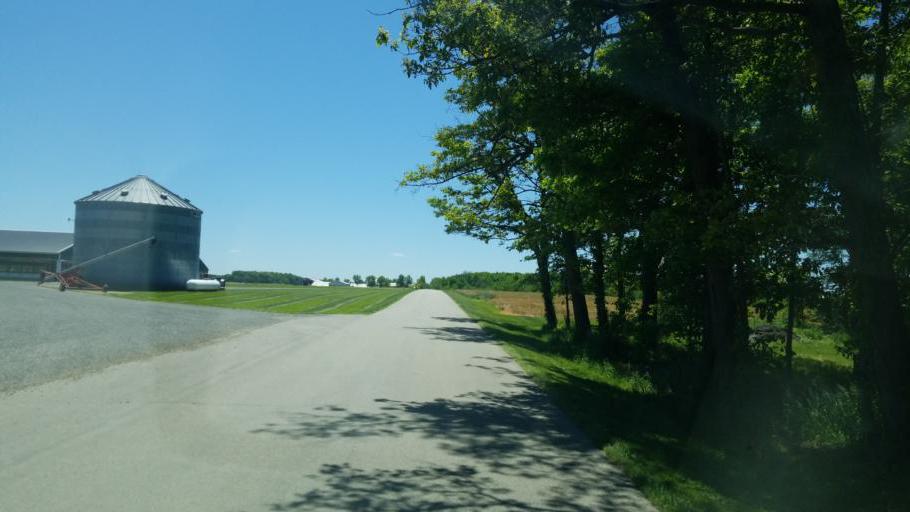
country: US
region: Ohio
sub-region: Mercer County
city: Fort Recovery
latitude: 40.3627
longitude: -84.8040
